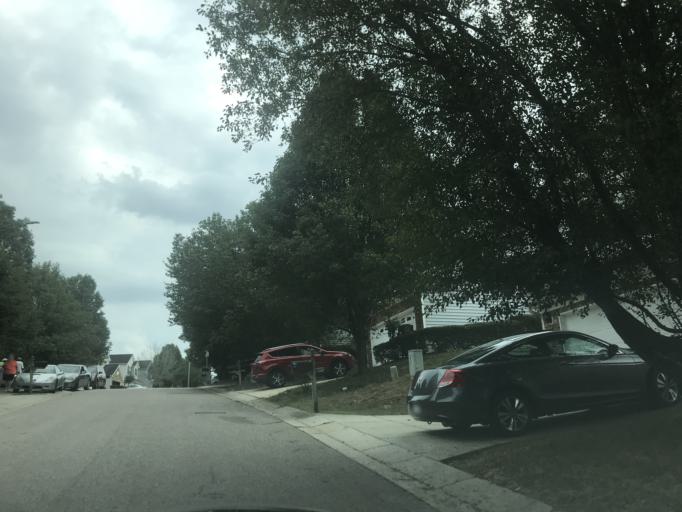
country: US
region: North Carolina
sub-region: Wake County
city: Knightdale
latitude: 35.8424
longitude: -78.5634
